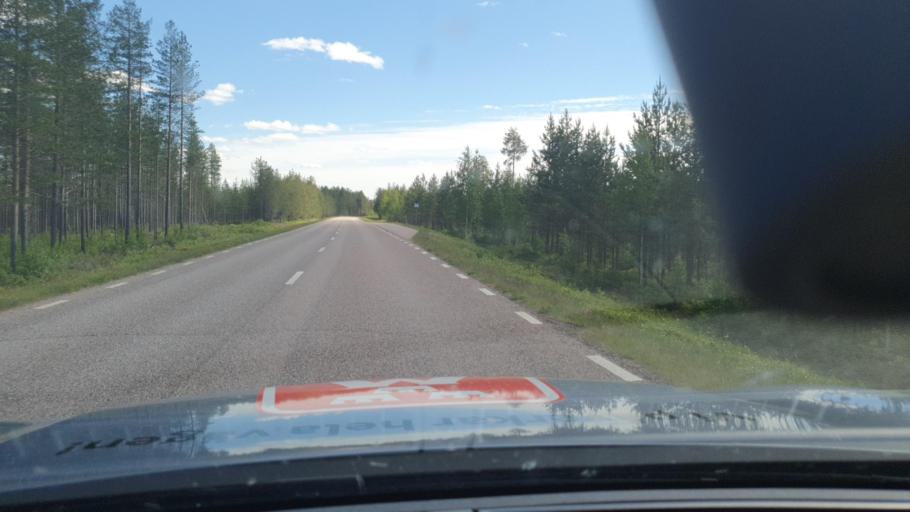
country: FI
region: Lapland
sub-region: Tunturi-Lappi
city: Kolari
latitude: 67.0394
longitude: 23.6976
